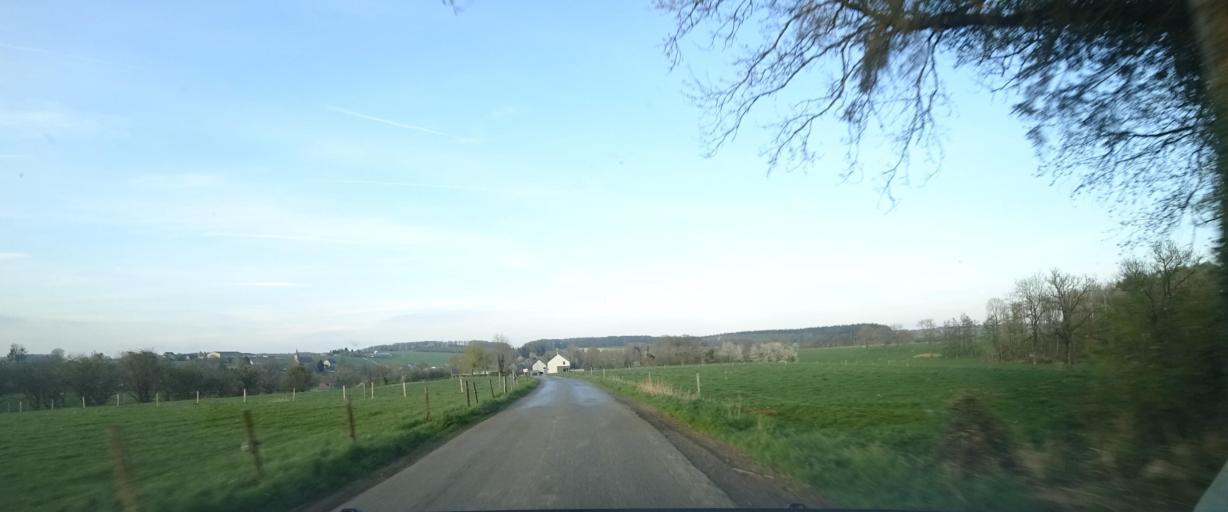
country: BE
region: Wallonia
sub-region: Province de Namur
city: Hamois
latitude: 50.3147
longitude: 5.1873
